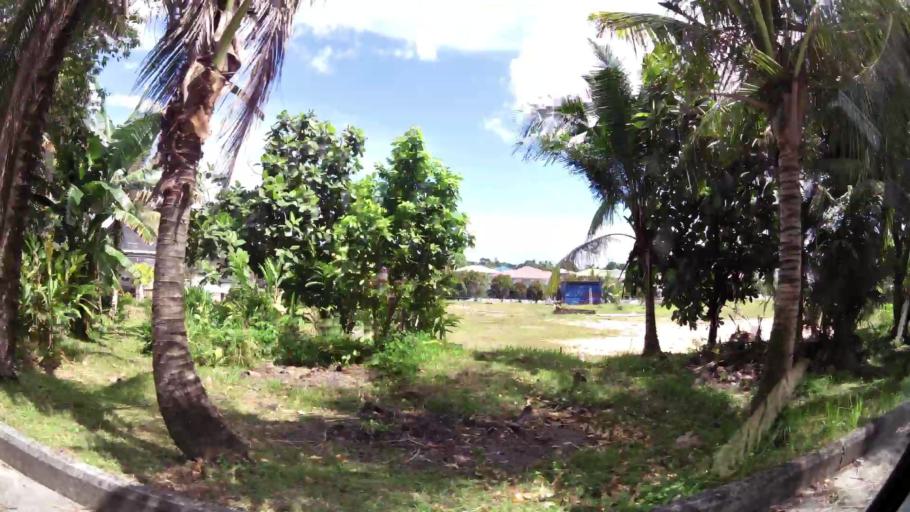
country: BN
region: Brunei and Muara
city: Bandar Seri Begawan
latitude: 4.9744
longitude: 114.9433
